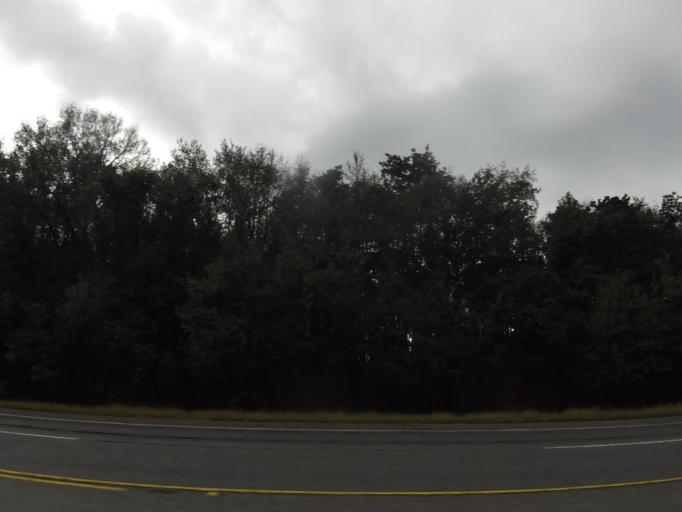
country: US
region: Georgia
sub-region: Wayne County
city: Jesup
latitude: 31.5812
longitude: -81.8539
